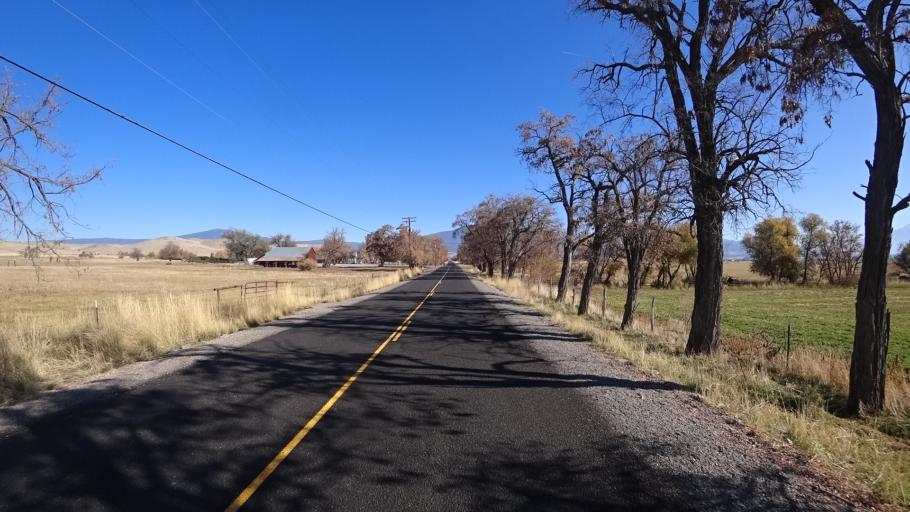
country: US
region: California
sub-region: Siskiyou County
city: Montague
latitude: 41.7263
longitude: -122.4127
